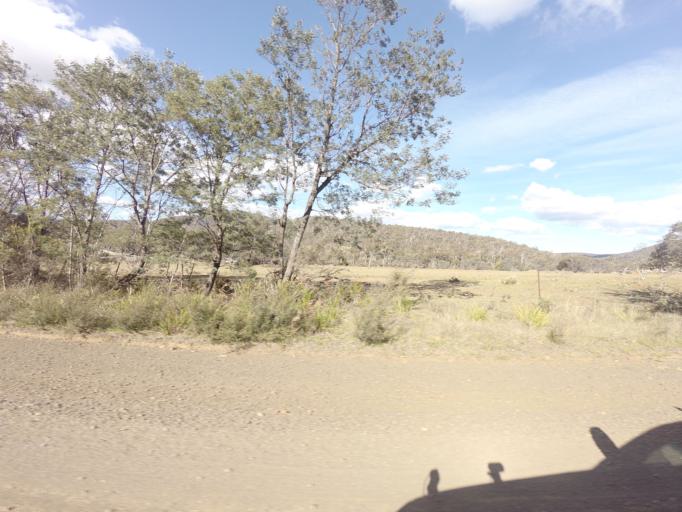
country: AU
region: Tasmania
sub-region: Break O'Day
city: St Helens
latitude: -41.8236
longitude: 148.0090
